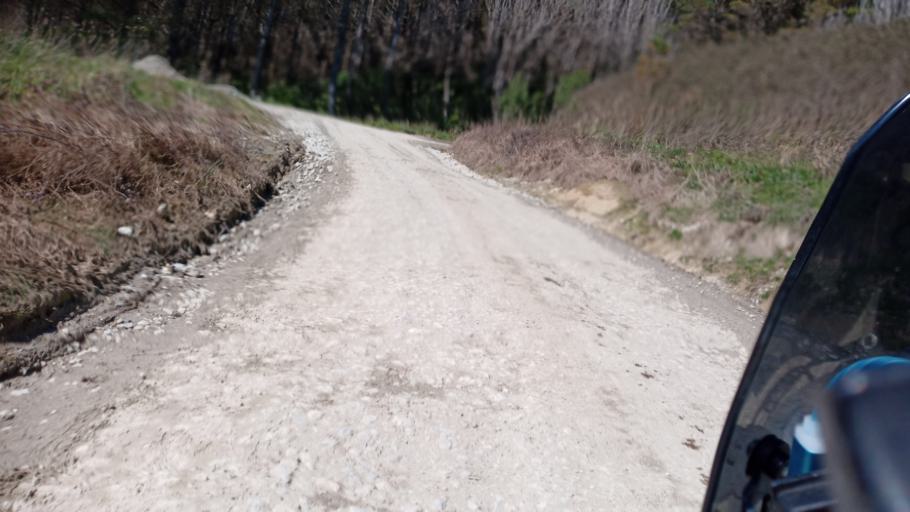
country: NZ
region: Gisborne
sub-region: Gisborne District
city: Gisborne
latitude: -38.8967
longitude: 177.8037
